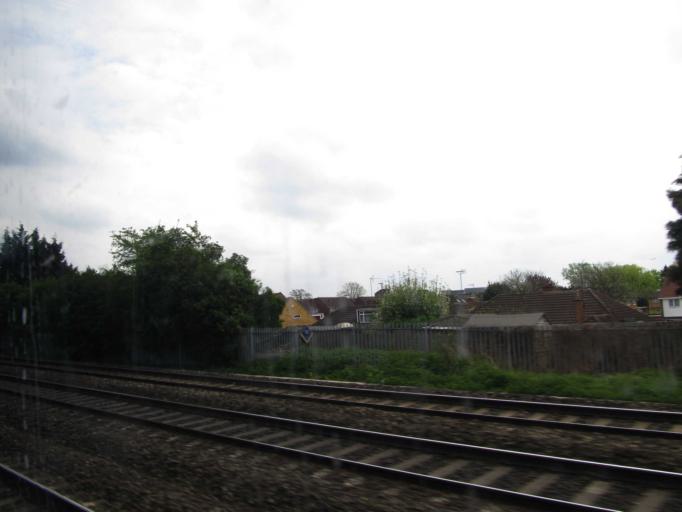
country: GB
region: England
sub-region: Royal Borough of Windsor and Maidenhead
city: Horton
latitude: 51.5081
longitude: -0.5477
